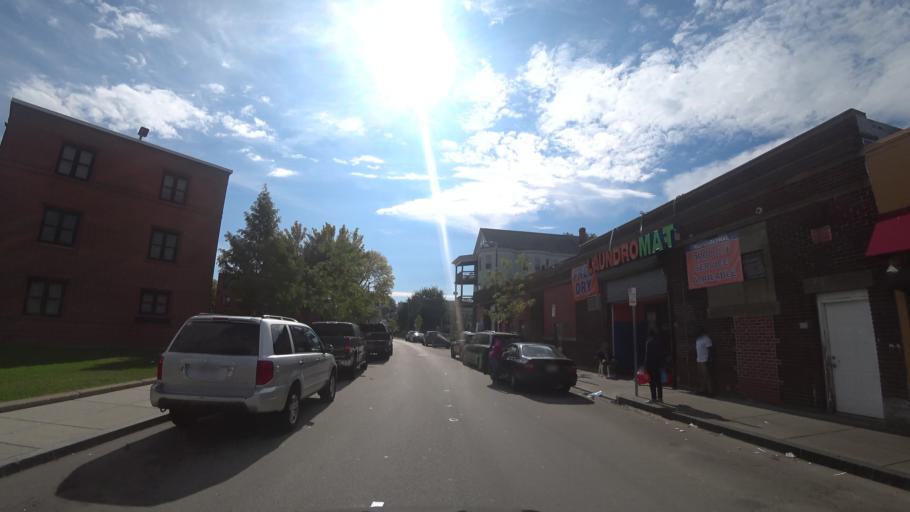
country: US
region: Massachusetts
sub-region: Suffolk County
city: Jamaica Plain
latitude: 42.2912
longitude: -71.0888
